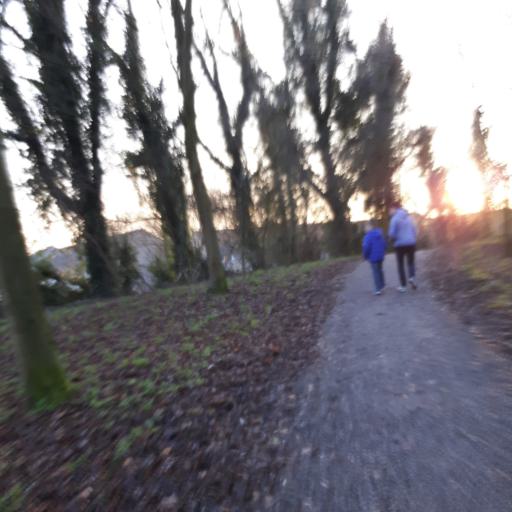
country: NL
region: Zeeland
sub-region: Gemeente Goes
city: Goes
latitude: 51.5192
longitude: 3.8811
